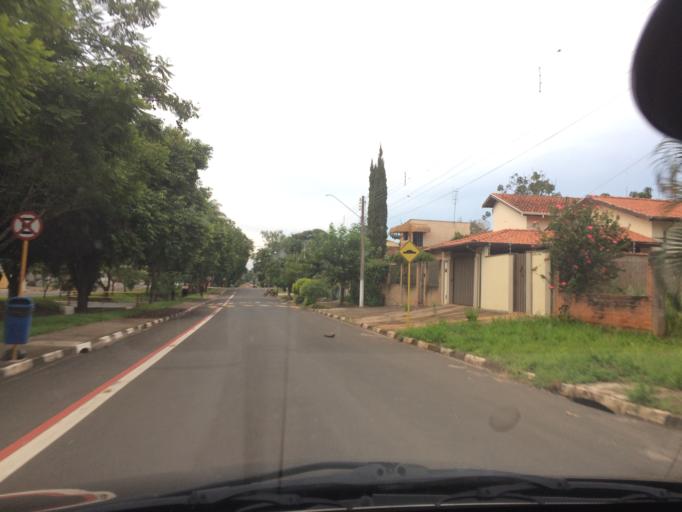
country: BR
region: Sao Paulo
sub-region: Casa Branca
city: Casa Branca
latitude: -21.7708
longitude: -47.0838
